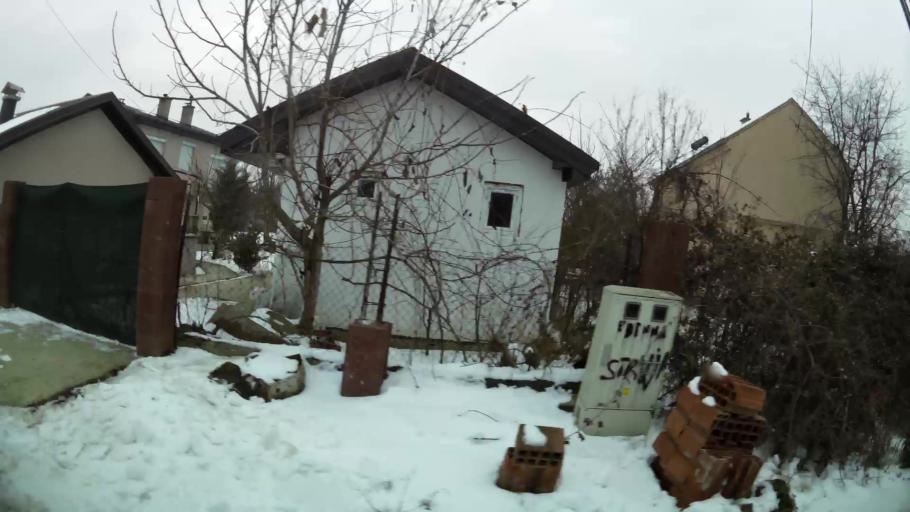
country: MK
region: Cucer-Sandevo
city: Chucher - Sandevo
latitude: 42.0497
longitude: 21.3593
